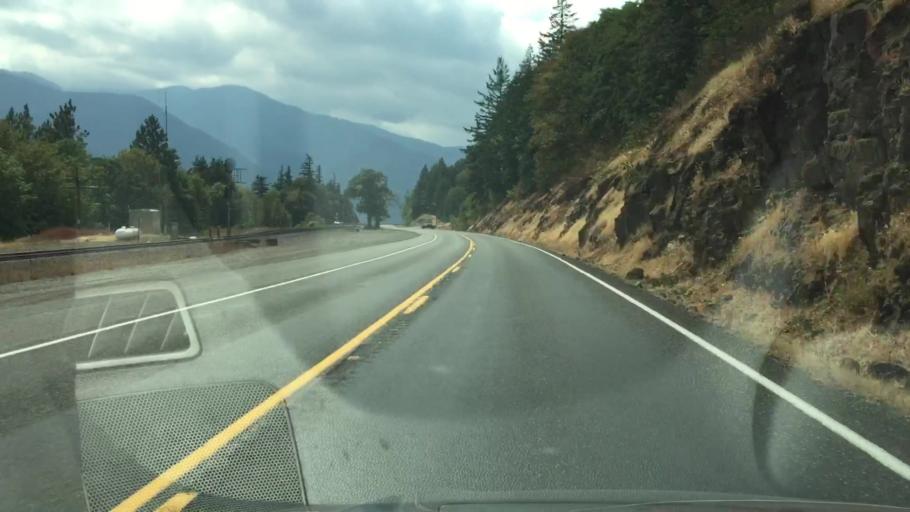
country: US
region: Oregon
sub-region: Hood River County
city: Hood River
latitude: 45.7111
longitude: -121.6561
